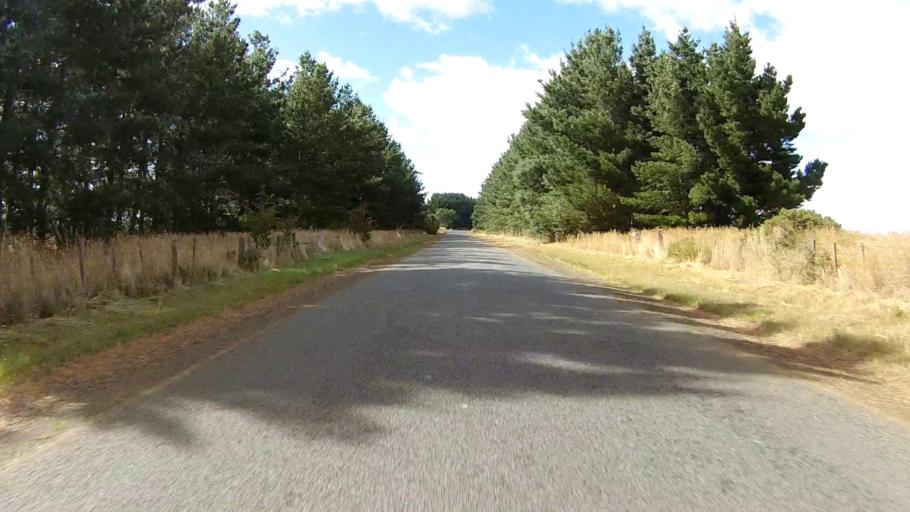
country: AU
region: Tasmania
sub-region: Northern Midlands
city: Evandale
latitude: -41.6917
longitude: 147.3644
